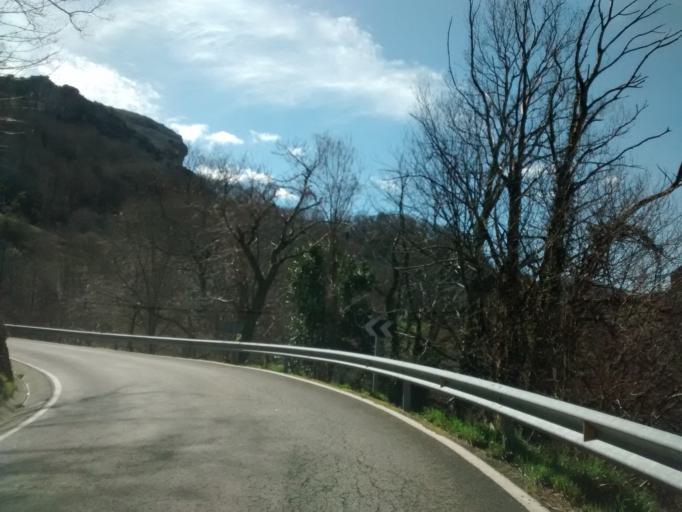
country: ES
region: Cantabria
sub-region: Provincia de Cantabria
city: Lierganes
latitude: 43.2685
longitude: -3.7096
